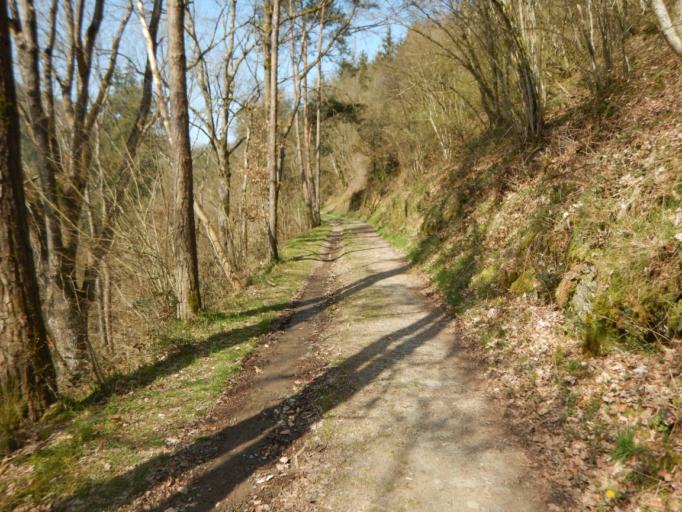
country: LU
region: Diekirch
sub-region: Canton de Diekirch
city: Bourscheid
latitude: 49.9510
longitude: 6.0656
